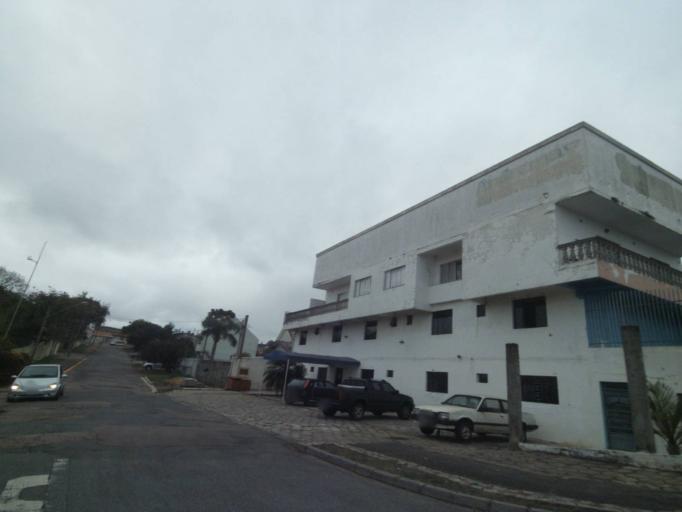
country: BR
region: Parana
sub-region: Curitiba
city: Curitiba
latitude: -25.5201
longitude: -49.3060
